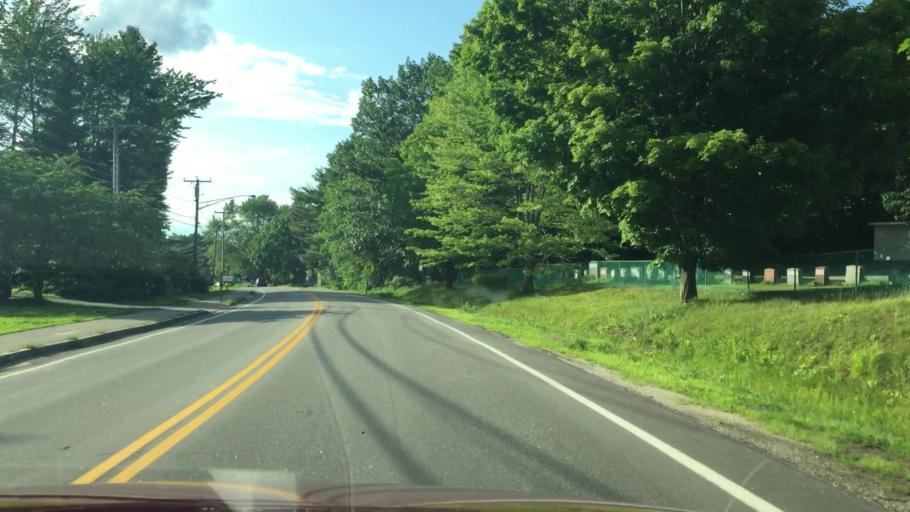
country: US
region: Maine
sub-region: Cumberland County
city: Westbrook
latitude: 43.6708
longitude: -70.3491
